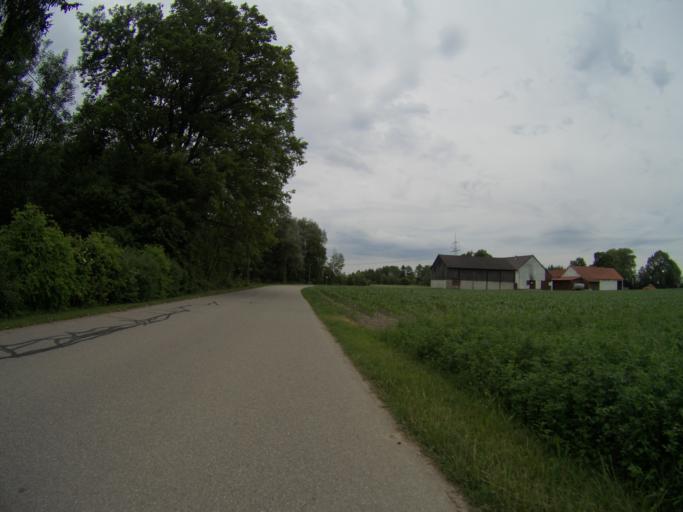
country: DE
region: Bavaria
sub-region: Upper Bavaria
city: Langenbach
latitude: 48.4067
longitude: 11.8622
